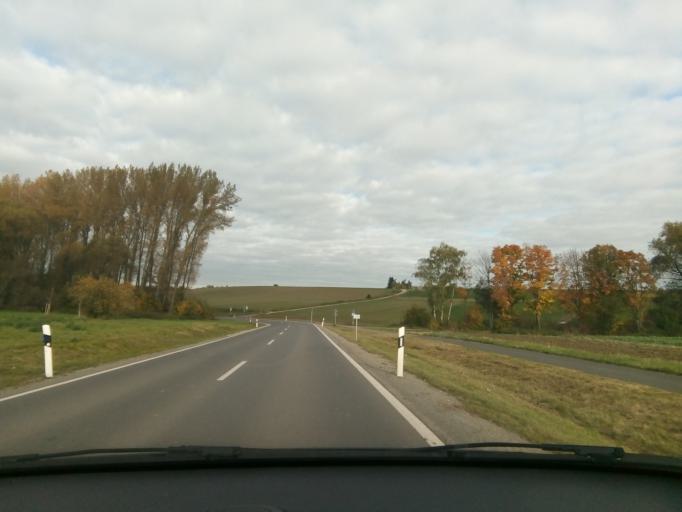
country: DE
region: Bavaria
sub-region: Regierungsbezirk Unterfranken
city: Gerolzhofen
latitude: 49.8892
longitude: 10.3641
